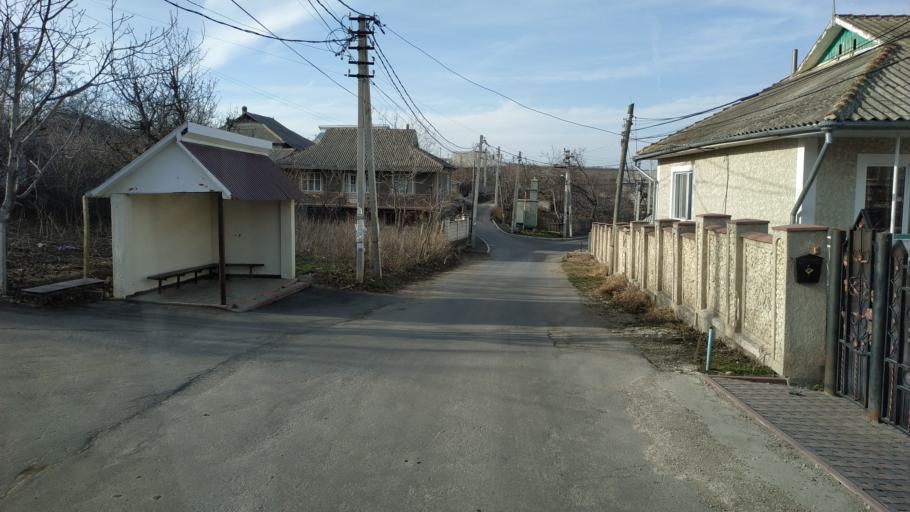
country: MD
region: Chisinau
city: Vatra
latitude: 47.0744
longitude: 28.6713
